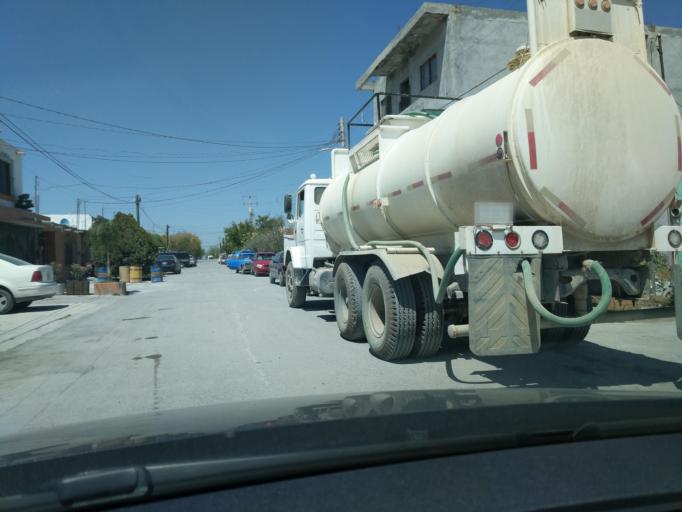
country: MX
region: Nuevo Leon
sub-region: Salinas Victoria
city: Emiliano Zapata
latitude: 25.9121
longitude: -100.2632
